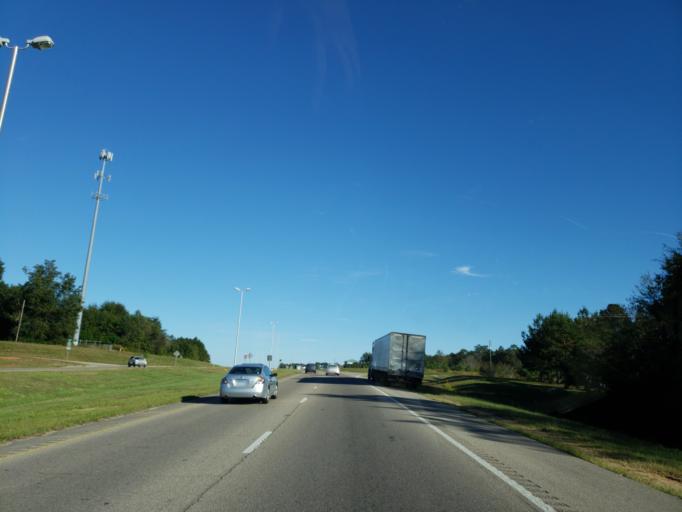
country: US
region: Mississippi
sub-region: Forrest County
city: Petal
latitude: 31.3533
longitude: -89.2514
